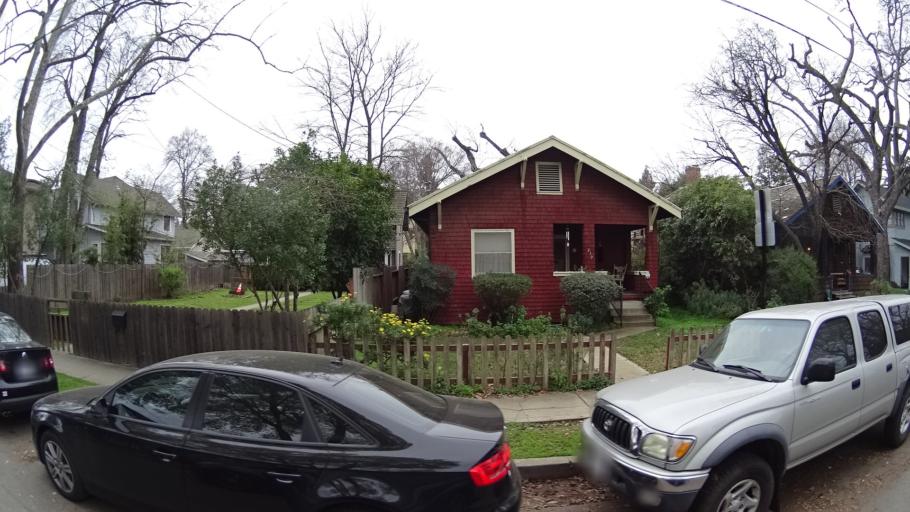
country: US
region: California
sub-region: Yolo County
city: Davis
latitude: 38.5430
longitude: -121.7458
